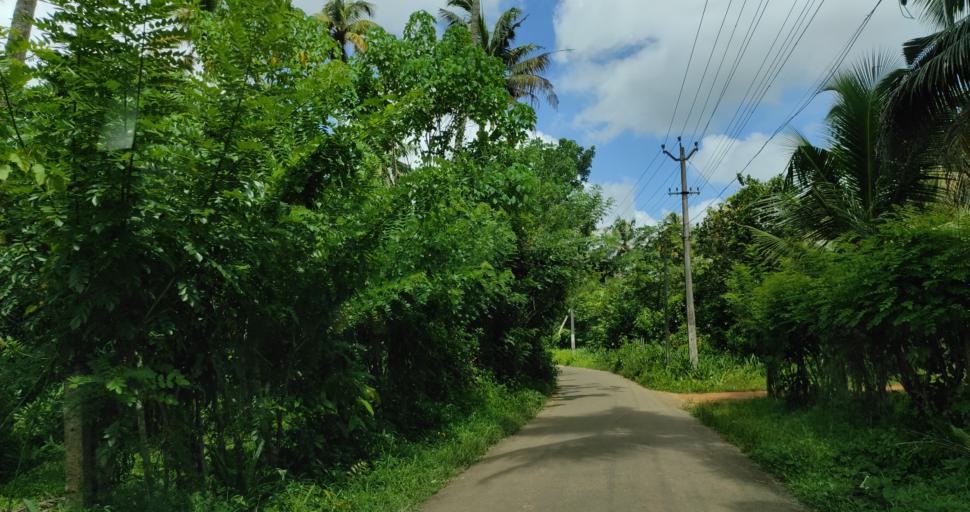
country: IN
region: Kerala
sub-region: Alappuzha
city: Shertallai
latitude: 9.6666
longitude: 76.3762
